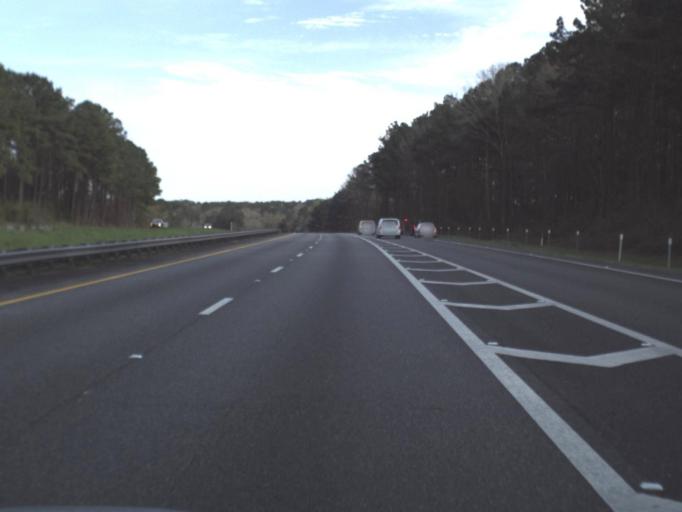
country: US
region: Florida
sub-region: Leon County
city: Tallahassee
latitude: 30.4816
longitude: -84.1530
